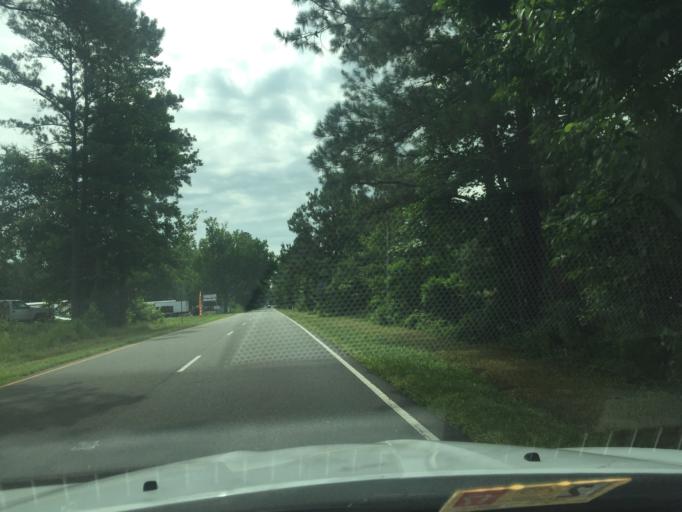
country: US
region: Virginia
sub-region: Charles City County
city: Charles City
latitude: 37.4485
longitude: -77.0700
